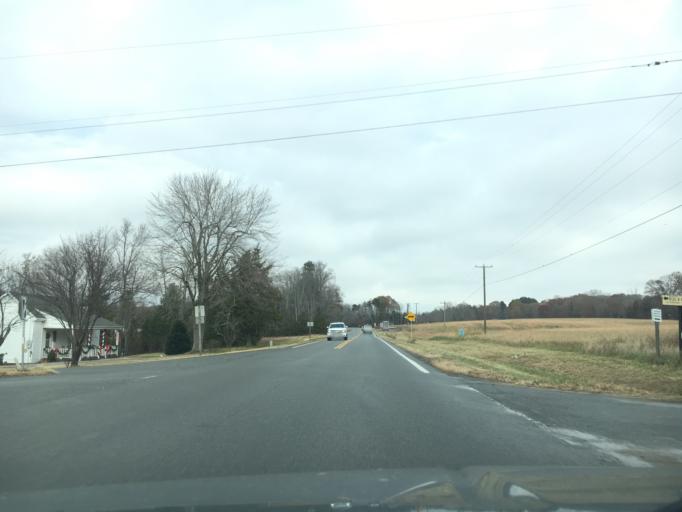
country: US
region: Virginia
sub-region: Prince Edward County
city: Farmville
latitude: 37.3663
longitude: -78.3726
